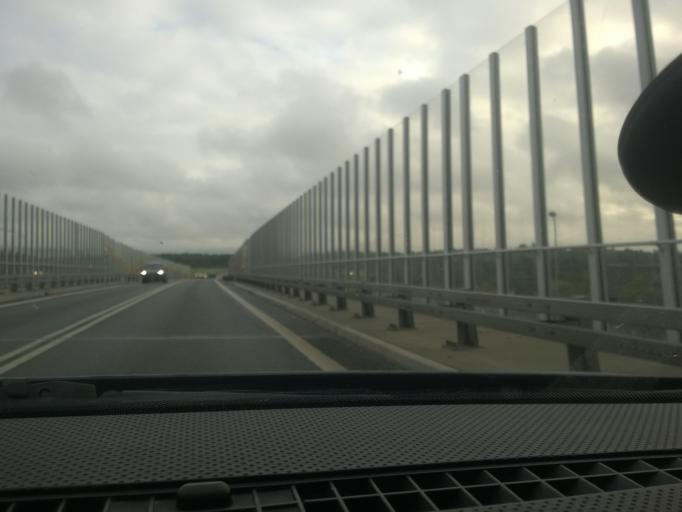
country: PL
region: Lodz Voivodeship
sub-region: Powiat sieradzki
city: Sieradz
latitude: 51.5653
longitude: 18.7081
